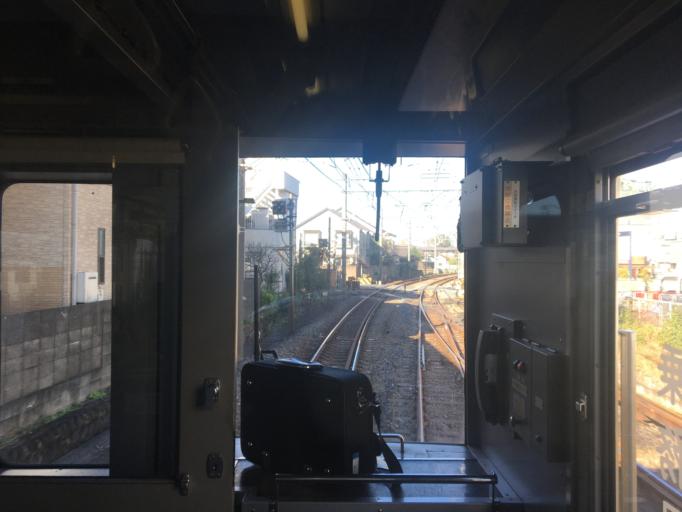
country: JP
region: Saitama
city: Sakado
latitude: 35.9573
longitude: 139.3913
